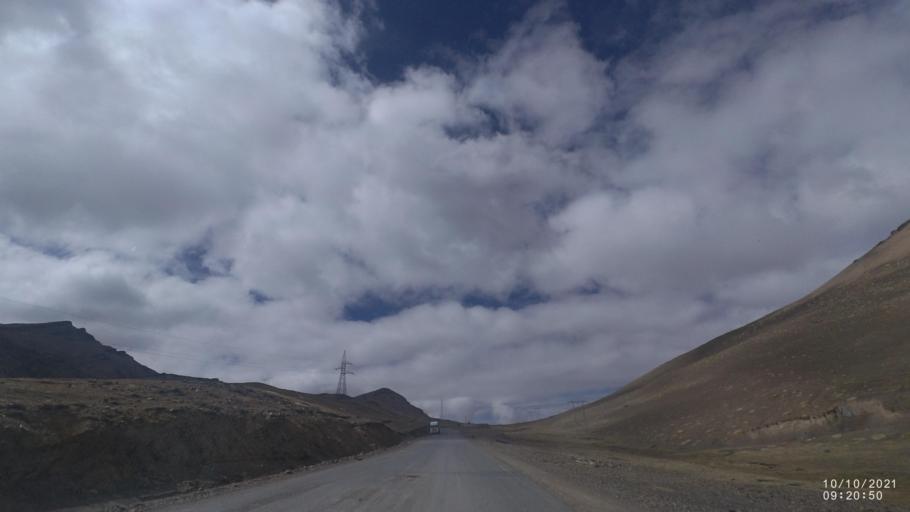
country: BO
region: La Paz
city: Quime
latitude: -17.0626
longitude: -67.2983
